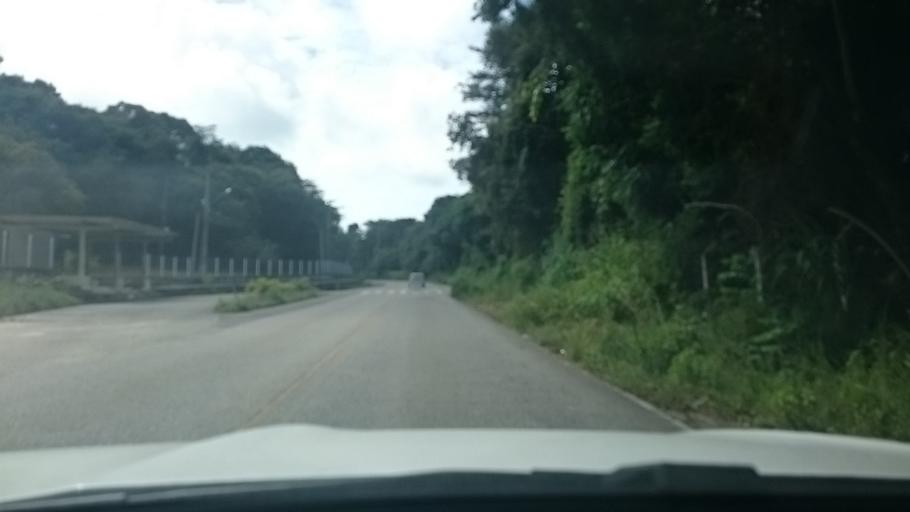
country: BR
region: Paraiba
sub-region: Joao Pessoa
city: Joao Pessoa
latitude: -7.1377
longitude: -34.8402
